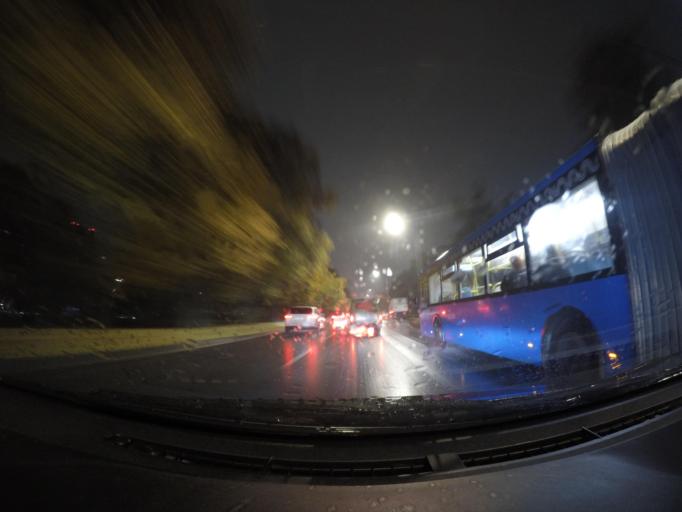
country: RU
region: Moscow
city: Kolomenskoye
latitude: 55.6737
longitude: 37.6633
